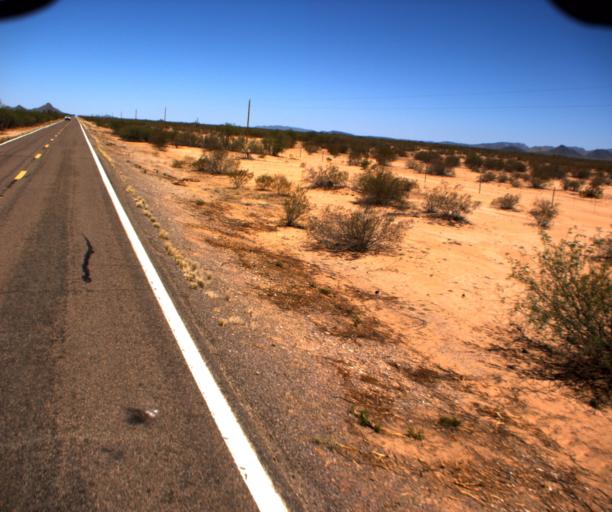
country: US
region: Arizona
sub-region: Pima County
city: Ajo
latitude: 32.1947
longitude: -112.4488
